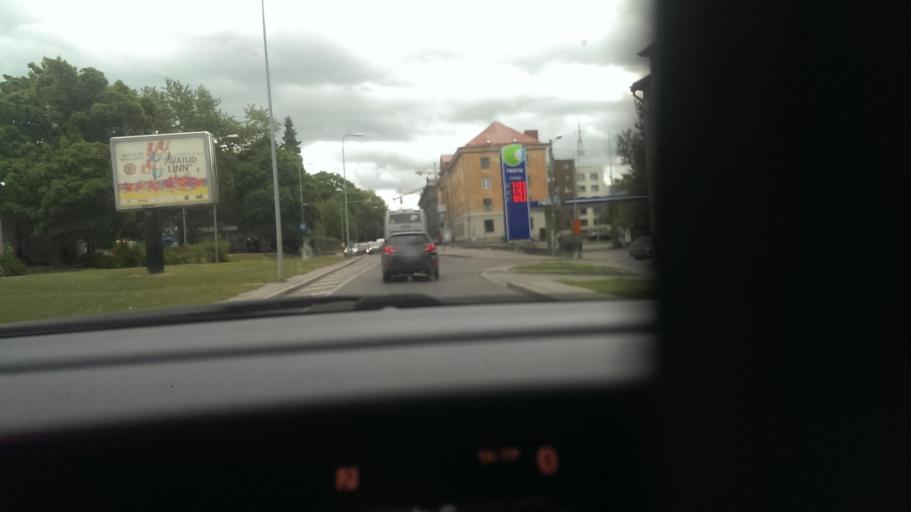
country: EE
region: Harju
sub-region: Tallinna linn
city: Tallinn
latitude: 59.4286
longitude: 24.7301
